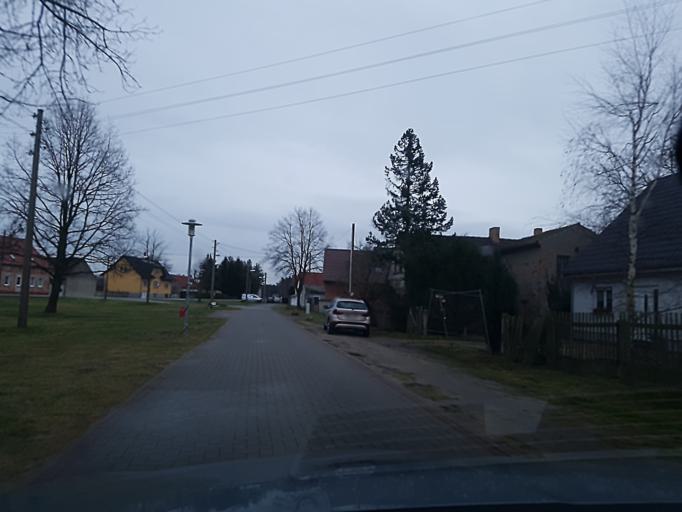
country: DE
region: Brandenburg
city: Schilda
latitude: 51.6024
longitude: 13.3445
